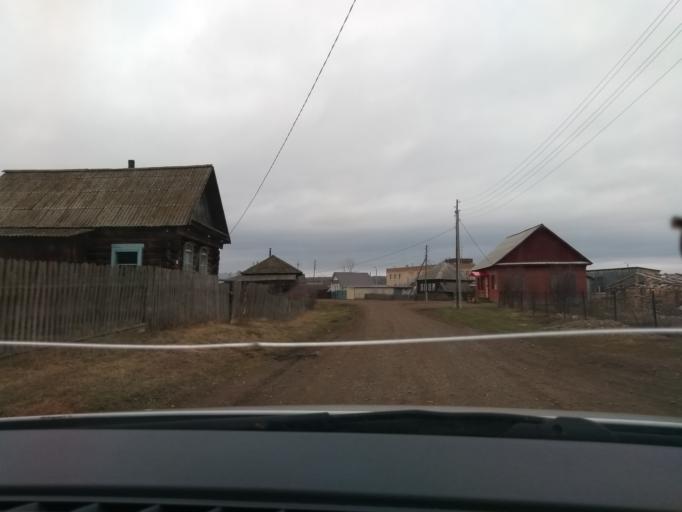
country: RU
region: Perm
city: Orda
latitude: 57.2143
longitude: 56.5957
